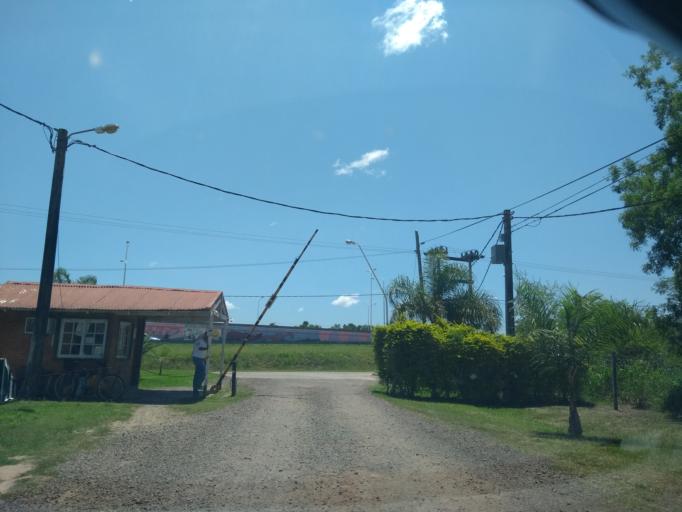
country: AR
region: Chaco
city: Resistencia
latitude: -27.4235
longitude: -58.9530
